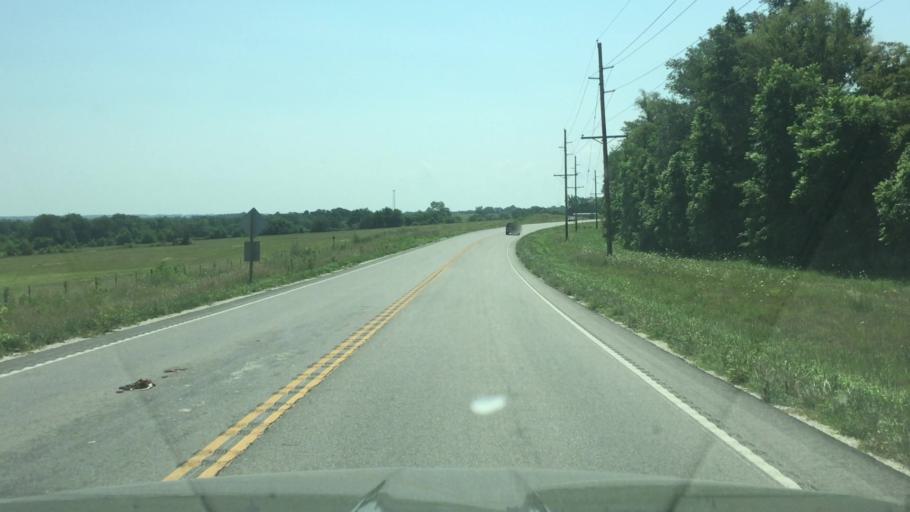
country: US
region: Missouri
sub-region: Miller County
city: Eldon
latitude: 38.3868
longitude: -92.6925
